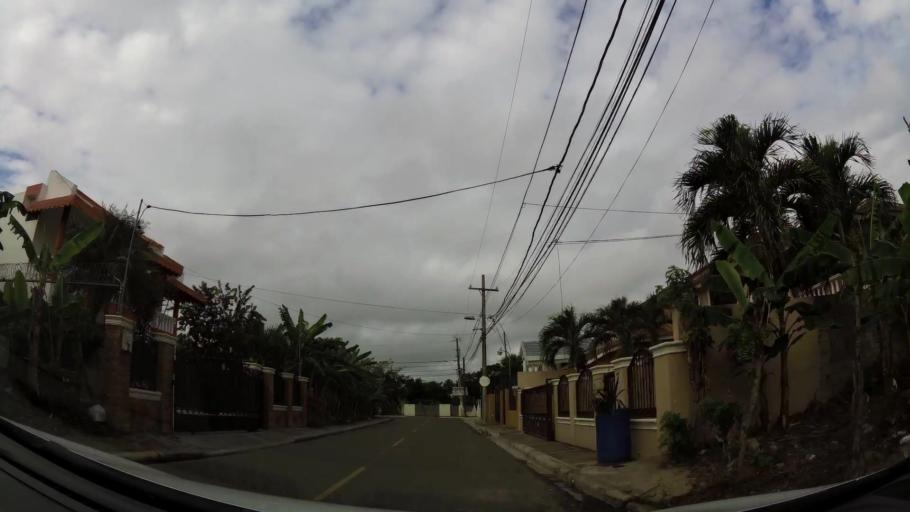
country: DO
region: Santiago
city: Santiago de los Caballeros
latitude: 19.4661
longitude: -70.6591
